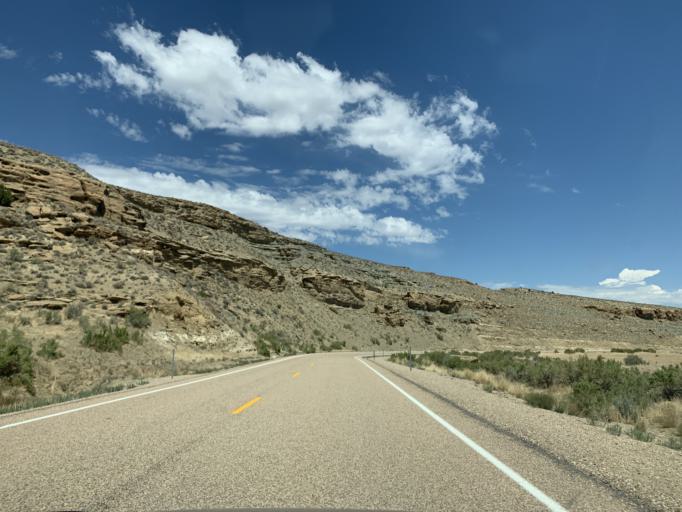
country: US
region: Utah
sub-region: Duchesne County
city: Duchesne
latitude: 40.0076
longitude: -110.1531
